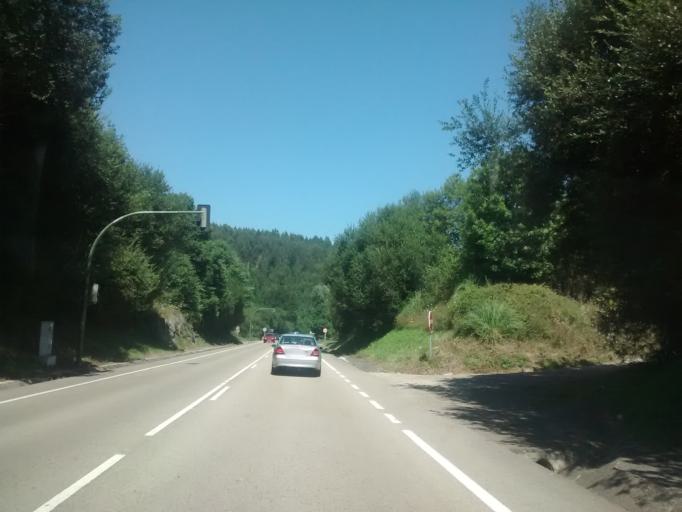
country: ES
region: Cantabria
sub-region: Provincia de Cantabria
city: Hazas de Cesto
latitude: 43.4238
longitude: -3.5689
